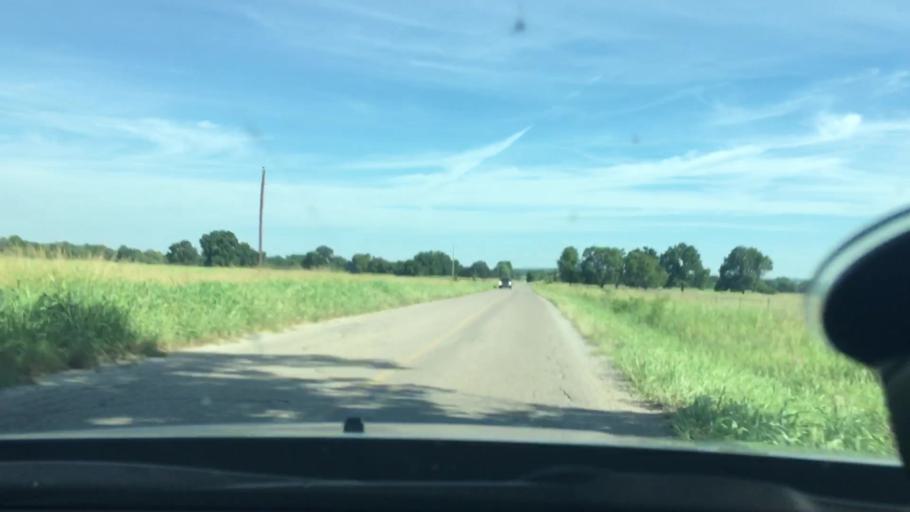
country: US
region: Oklahoma
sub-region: Carter County
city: Lone Grove
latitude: 34.2972
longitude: -97.2824
